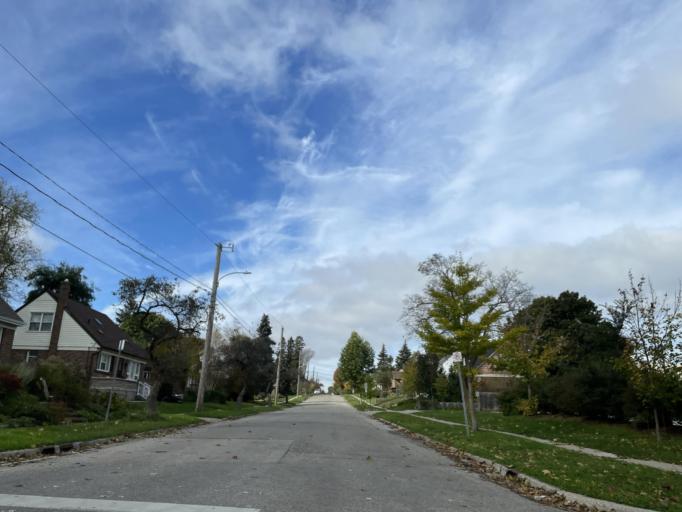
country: CA
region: Ontario
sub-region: Wellington County
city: Guelph
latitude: 43.5372
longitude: -80.2679
